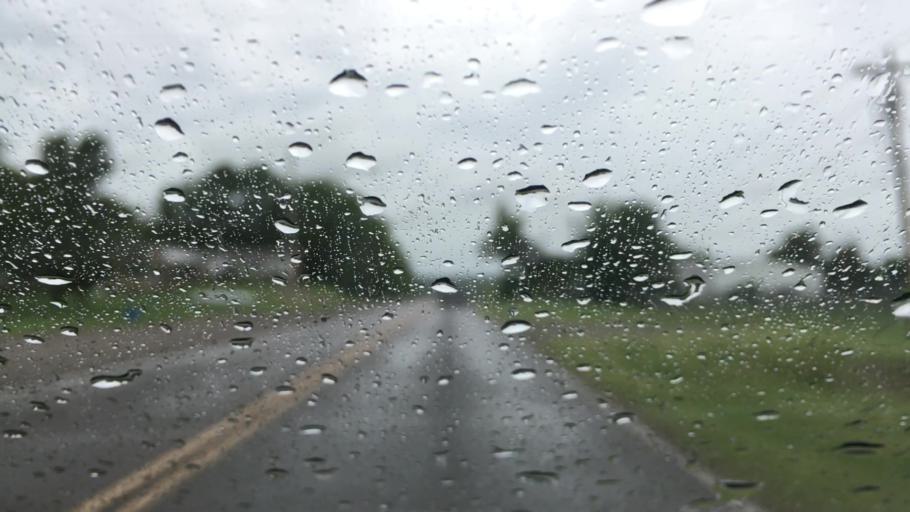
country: US
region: Oklahoma
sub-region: Cherokee County
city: Tahlequah
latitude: 35.9175
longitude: -94.9921
